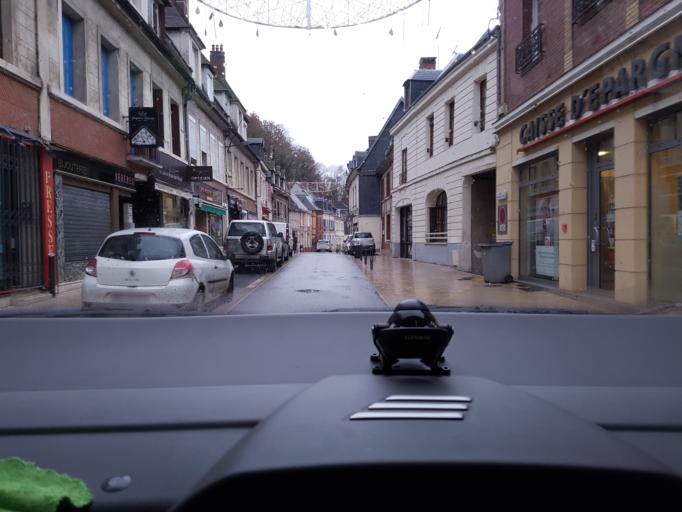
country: FR
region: Haute-Normandie
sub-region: Departement de l'Eure
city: Beaumont-le-Roger
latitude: 49.0813
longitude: 0.7788
